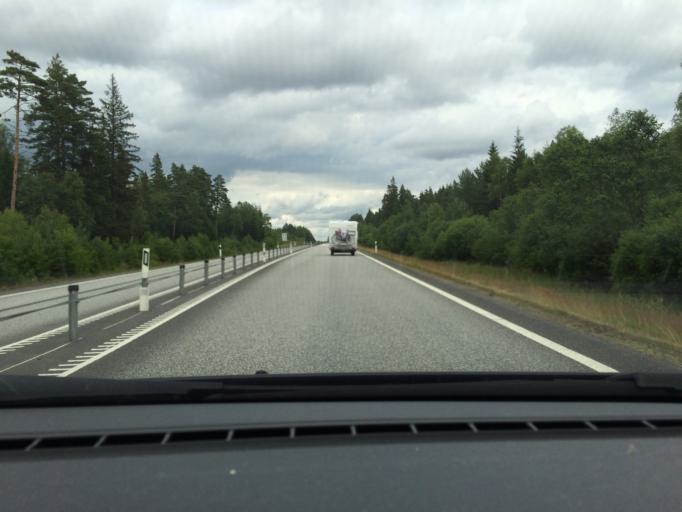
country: SE
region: Joenkoeping
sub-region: Varnamo Kommun
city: Forsheda
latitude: 57.1694
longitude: 13.8955
